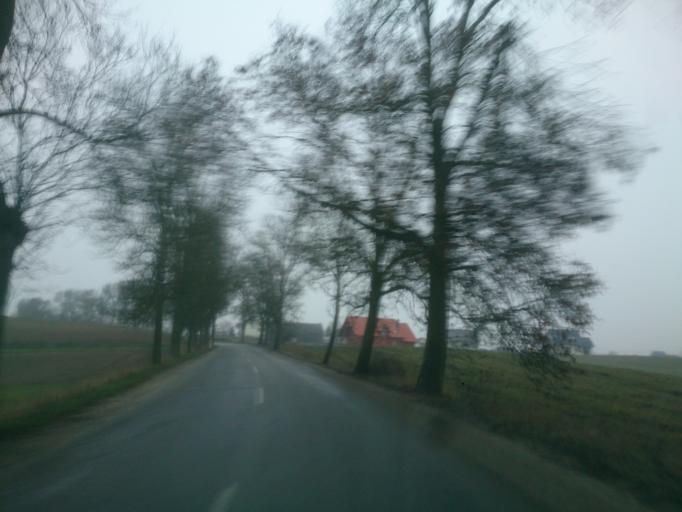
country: PL
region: Pomeranian Voivodeship
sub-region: Powiat starogardzki
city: Lubichowo
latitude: 53.8419
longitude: 18.4299
